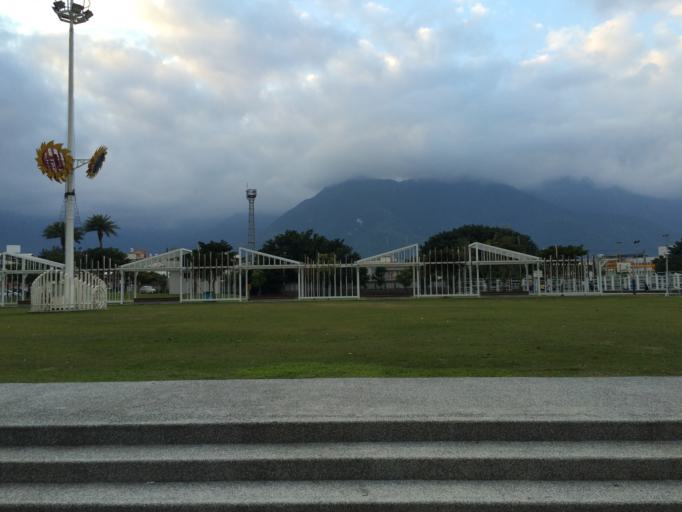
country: TW
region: Taiwan
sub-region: Hualien
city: Hualian
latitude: 23.9895
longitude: 121.6008
